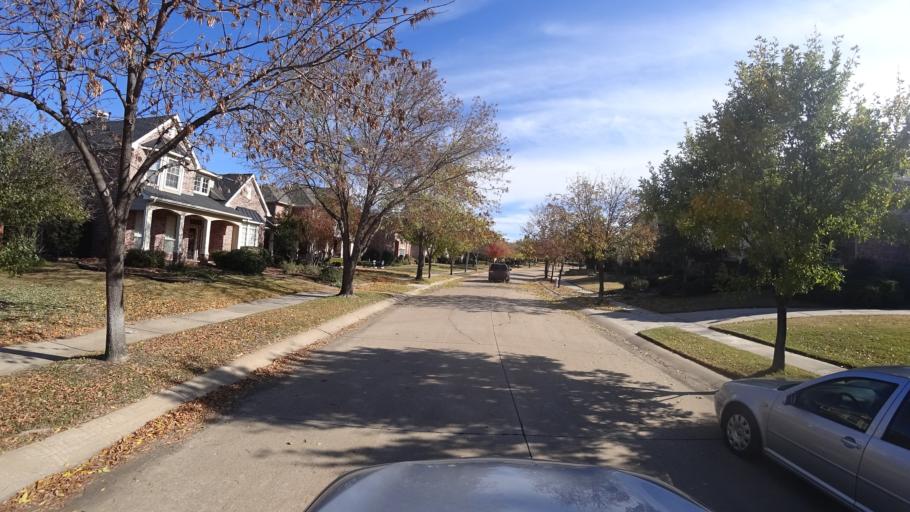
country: US
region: Texas
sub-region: Denton County
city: The Colony
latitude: 33.0327
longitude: -96.9004
